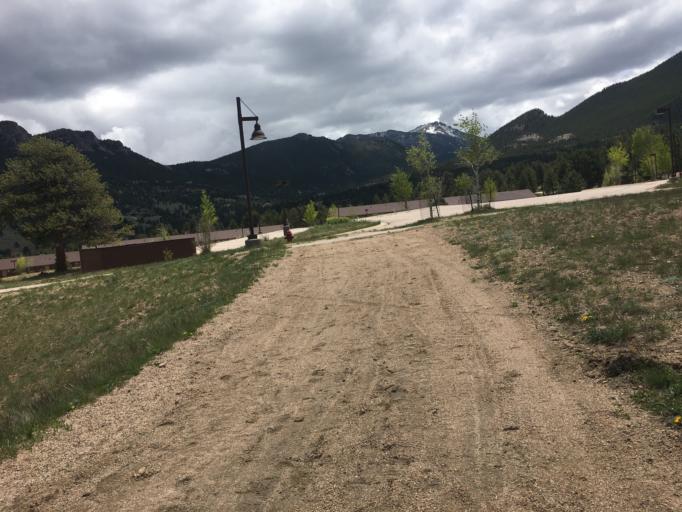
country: US
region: Colorado
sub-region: Larimer County
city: Estes Park
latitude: 40.3385
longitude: -105.5746
